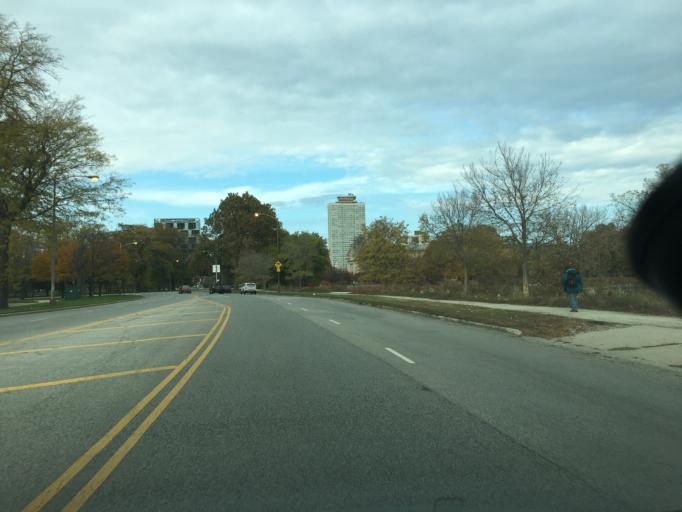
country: US
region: Illinois
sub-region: Cook County
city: Chicago
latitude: 41.7865
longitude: -87.5849
